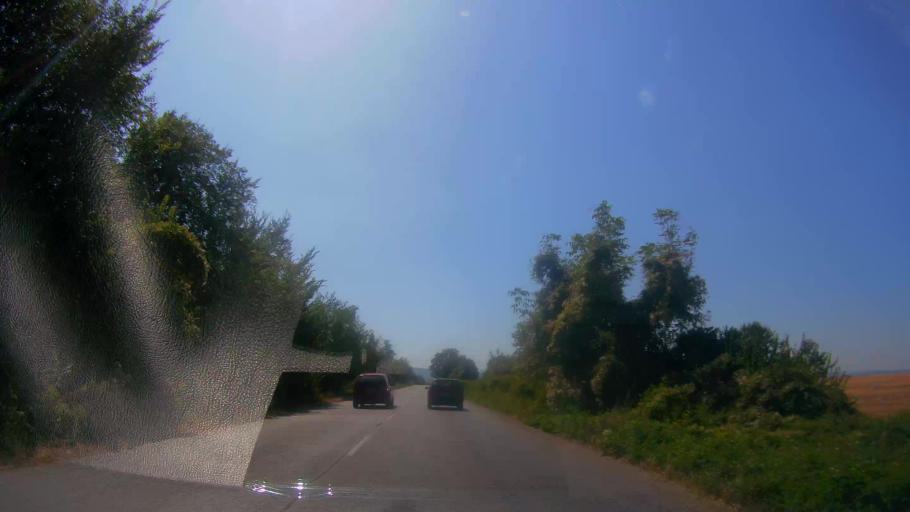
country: BG
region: Veliko Turnovo
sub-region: Obshtina Gorna Oryakhovitsa
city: Purvomaytsi
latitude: 43.2335
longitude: 25.6404
